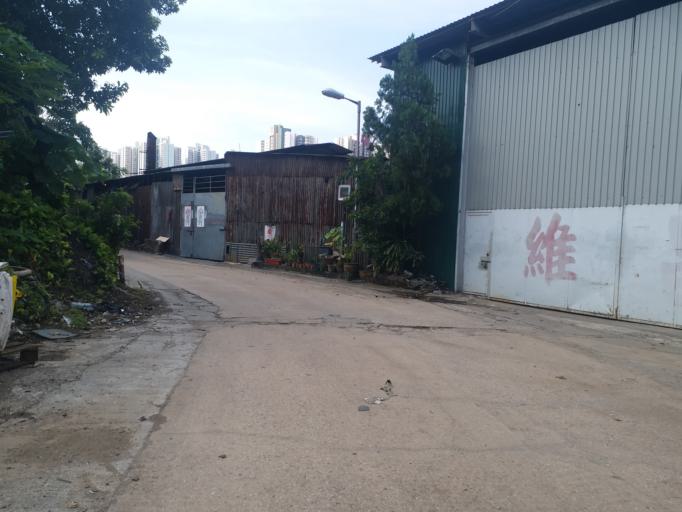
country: HK
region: Yuen Long
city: Yuen Long Kau Hui
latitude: 22.4404
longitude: 114.0020
